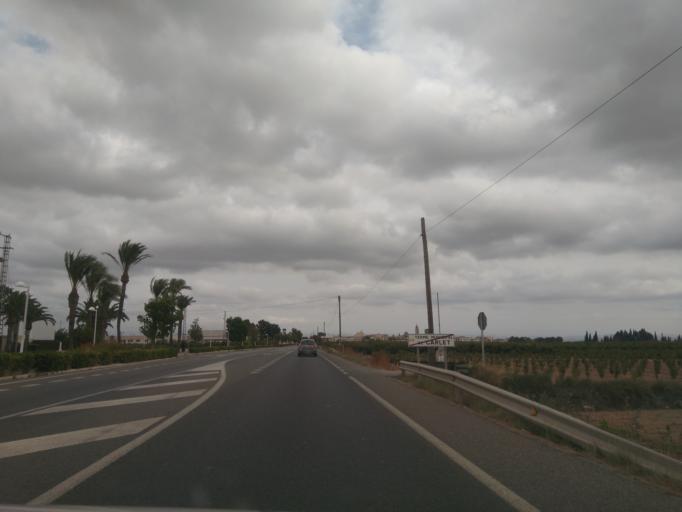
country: ES
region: Valencia
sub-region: Provincia de Valencia
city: L'Alcudia
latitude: 39.2093
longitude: -0.5110
